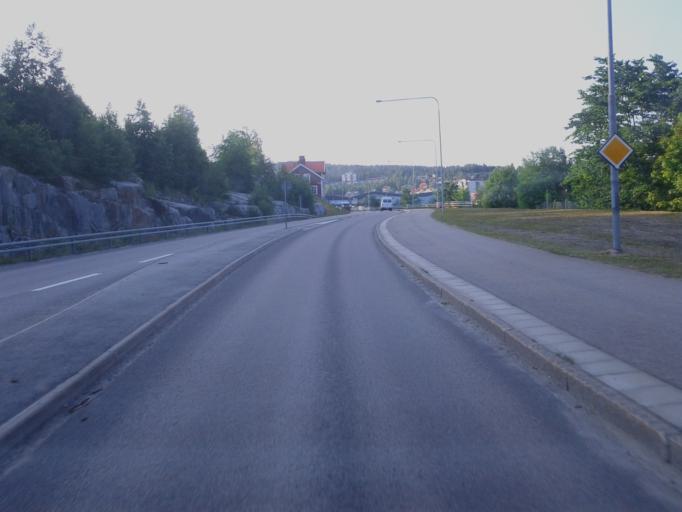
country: SE
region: Vaesternorrland
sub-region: OErnskoeldsviks Kommun
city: Ornskoldsvik
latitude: 63.2845
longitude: 18.7080
